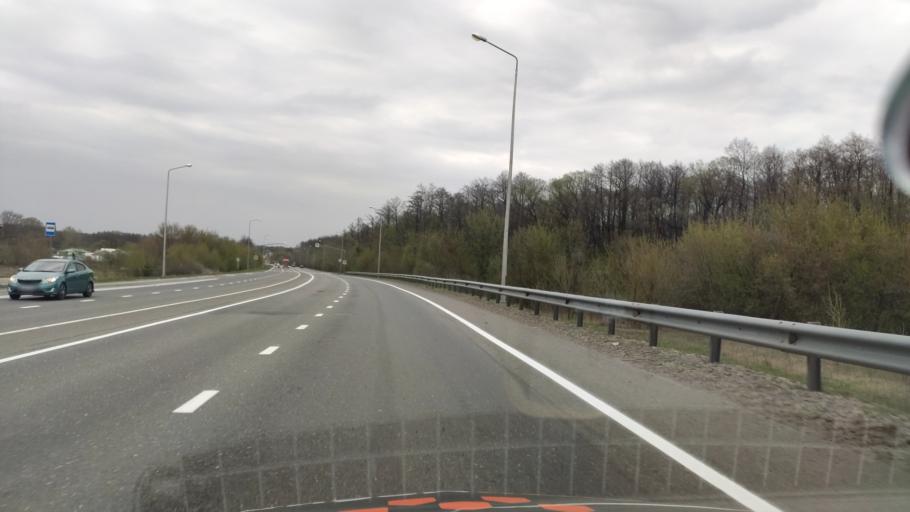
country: RU
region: Belgorod
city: Staryy Oskol
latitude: 51.3474
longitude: 37.8236
